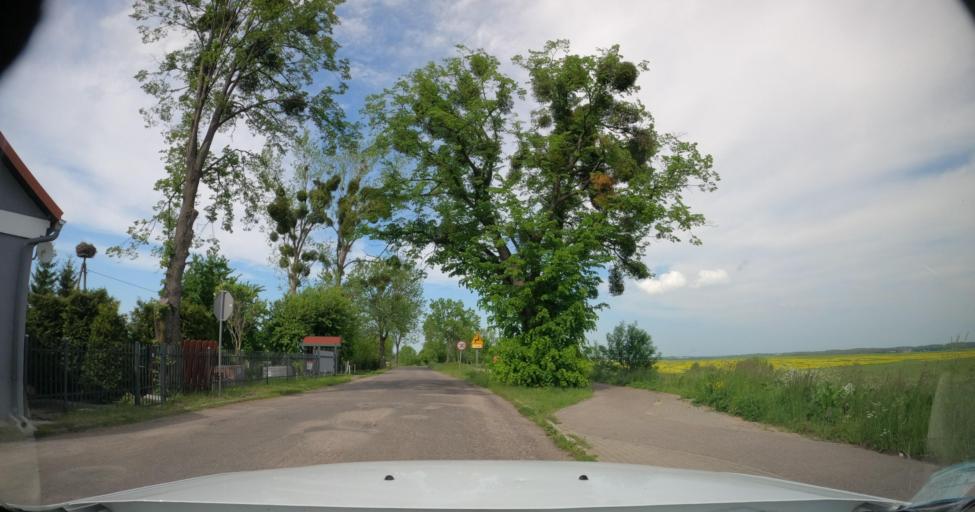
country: PL
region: Warmian-Masurian Voivodeship
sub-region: Powiat lidzbarski
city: Lidzbark Warminski
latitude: 54.1484
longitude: 20.5582
